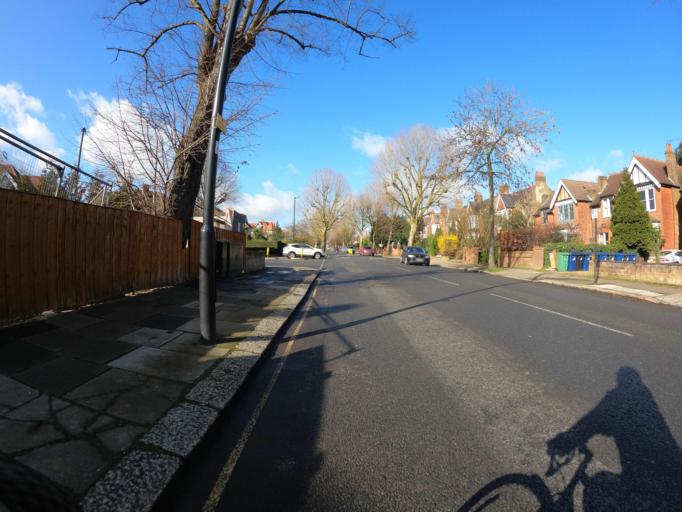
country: GB
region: England
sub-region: Greater London
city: Ealing
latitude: 51.5178
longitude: -0.3227
